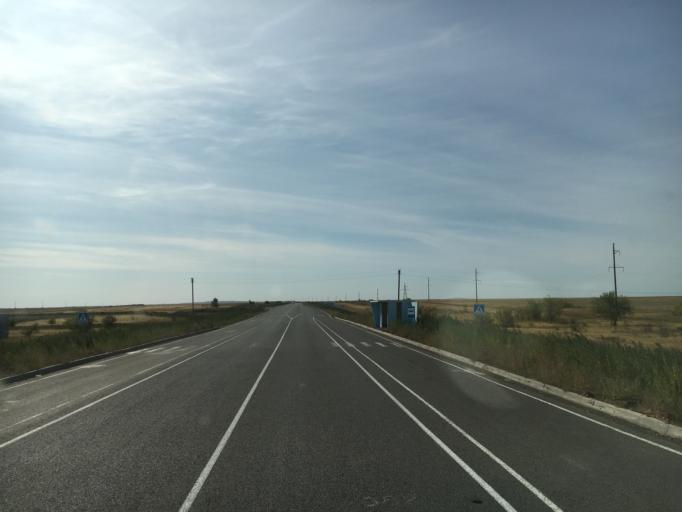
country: KZ
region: Batys Qazaqstan
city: Peremetnoe
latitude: 51.1202
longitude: 50.7427
